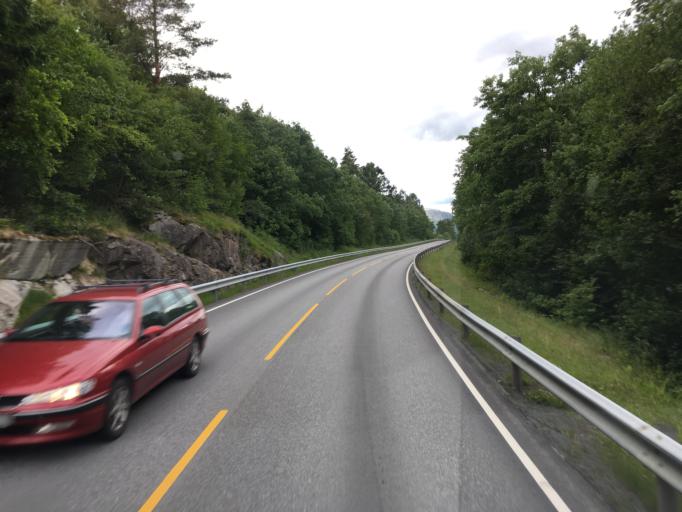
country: NO
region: More og Romsdal
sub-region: Sunndal
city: Sunndalsora
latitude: 62.6436
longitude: 8.7162
